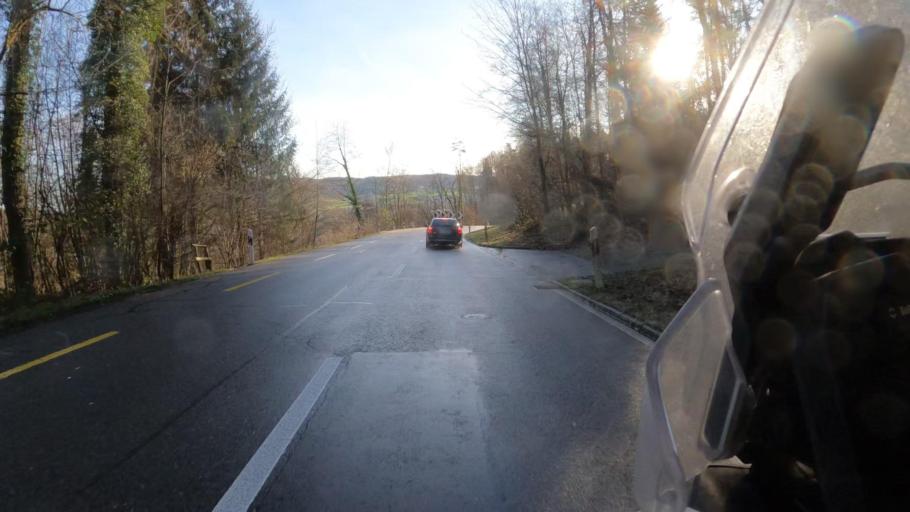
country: CH
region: Zurich
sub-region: Bezirk Buelach
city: Embrach / Kellersacker
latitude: 47.5166
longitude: 8.5799
